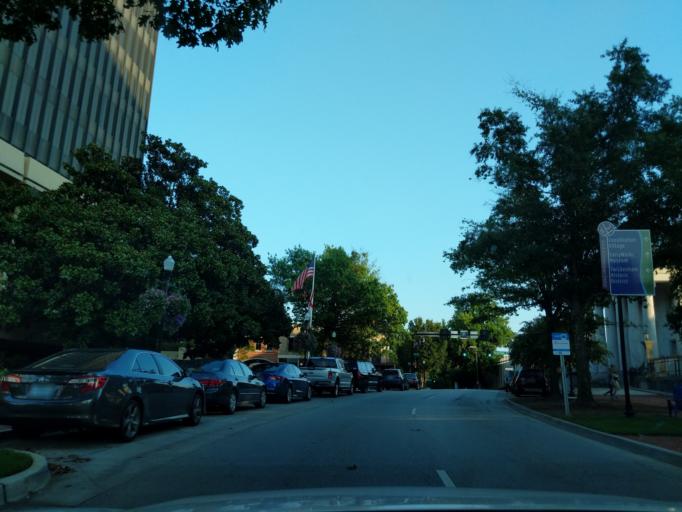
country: US
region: Alabama
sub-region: Madison County
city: Huntsville
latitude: 34.7302
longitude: -86.5857
